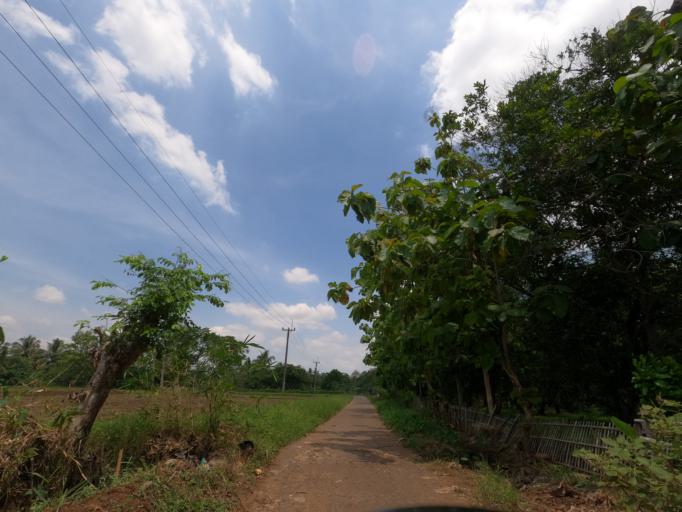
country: ID
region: West Java
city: Pamanukan
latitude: -6.5075
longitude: 107.7708
